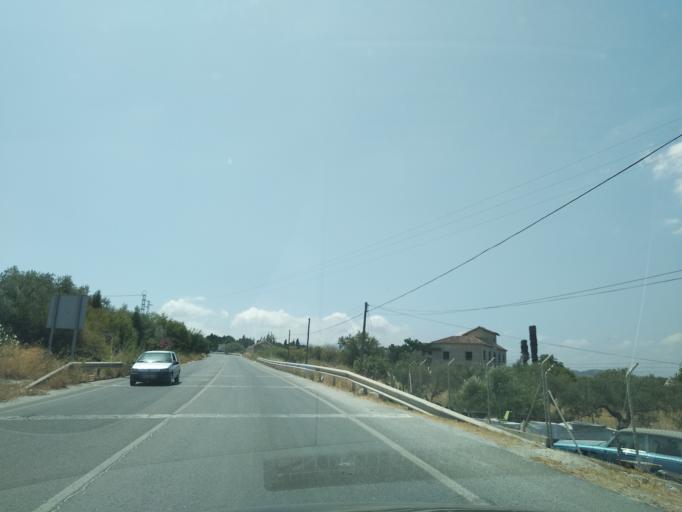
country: ES
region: Andalusia
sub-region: Provincia de Malaga
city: Alhaurin el Grande
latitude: 36.6553
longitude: -4.6772
